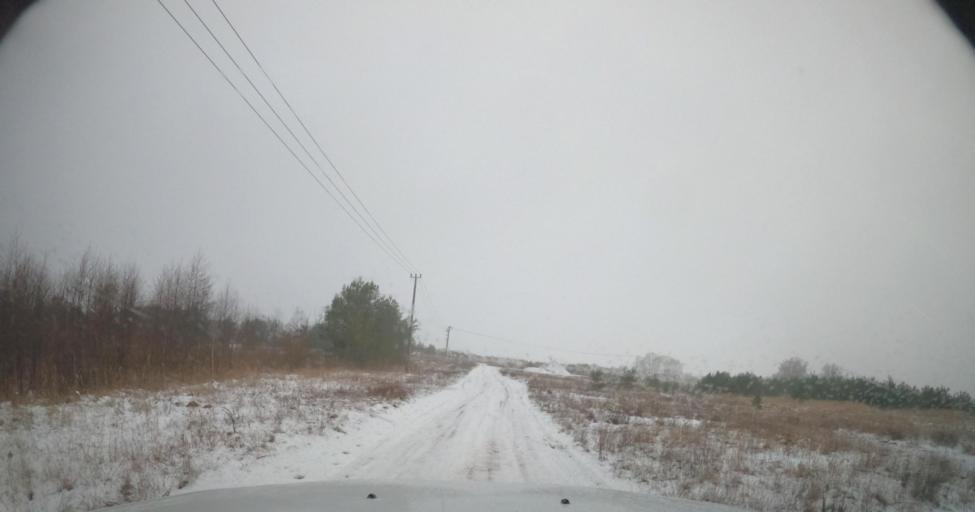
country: PL
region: West Pomeranian Voivodeship
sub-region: Powiat kamienski
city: Golczewo
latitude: 53.7815
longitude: 14.9576
